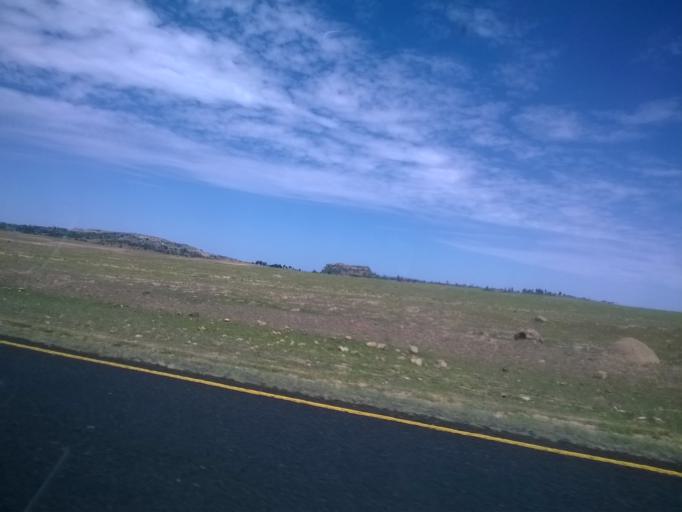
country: LS
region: Berea
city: Teyateyaneng
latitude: -29.0946
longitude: 27.8550
